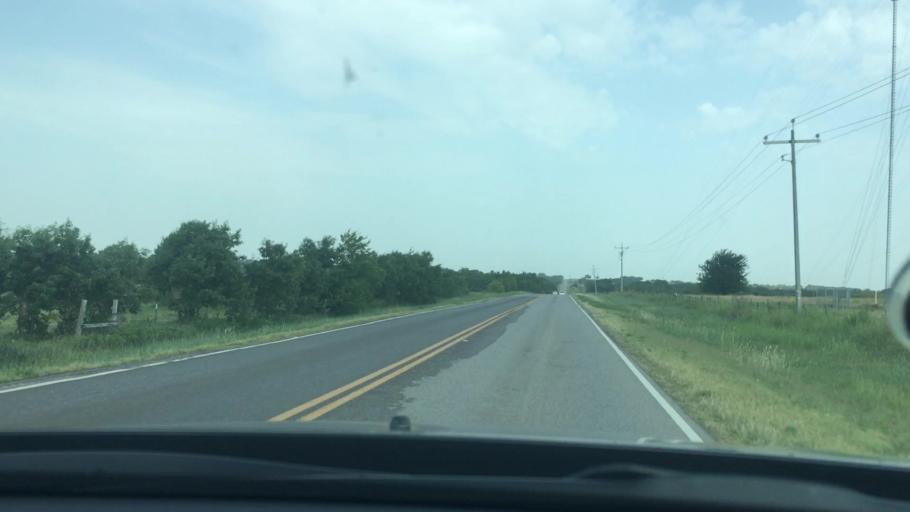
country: US
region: Oklahoma
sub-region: Garvin County
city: Stratford
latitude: 34.7967
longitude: -96.8818
